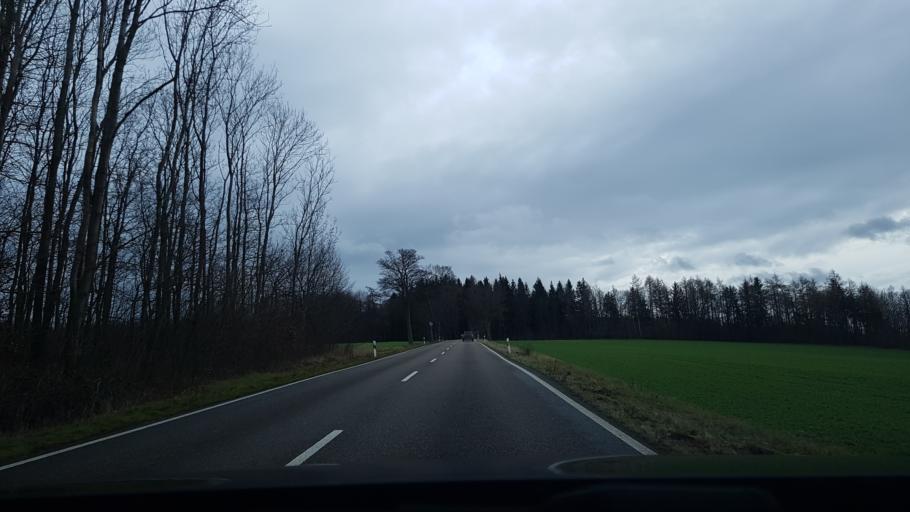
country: DE
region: Saxony
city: Dohma
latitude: 50.8553
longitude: 13.9547
